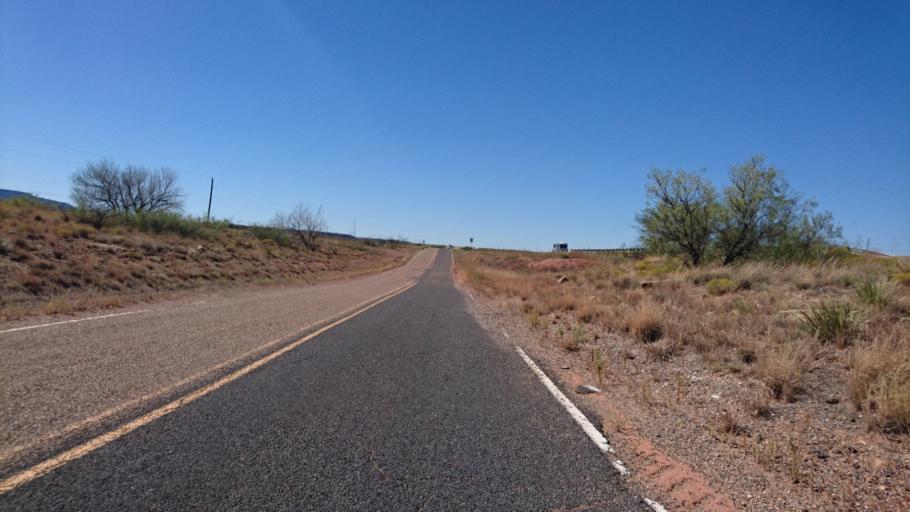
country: US
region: New Mexico
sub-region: Quay County
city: Tucumcari
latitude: 35.0860
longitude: -104.0987
